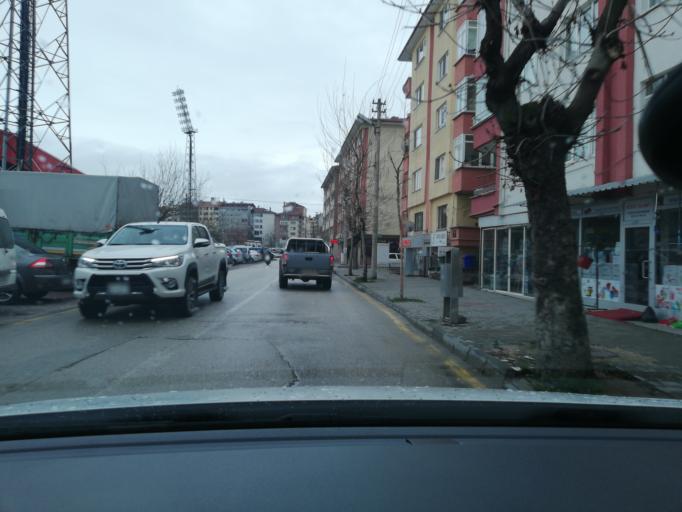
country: TR
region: Bolu
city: Bolu
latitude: 40.7369
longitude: 31.6056
